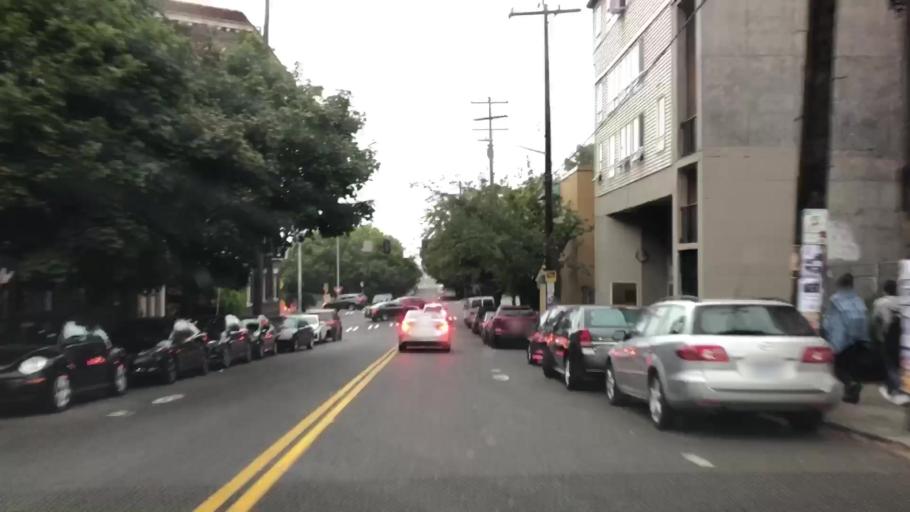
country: US
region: Washington
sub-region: Kitsap County
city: Bainbridge Island
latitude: 47.5820
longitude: -122.4932
